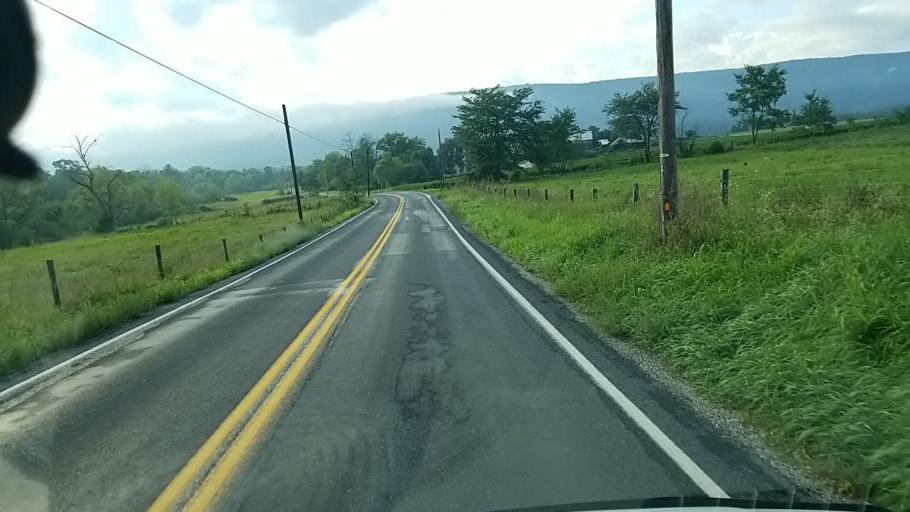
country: US
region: Pennsylvania
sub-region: Cumberland County
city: Newville
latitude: 40.1946
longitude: -77.4955
